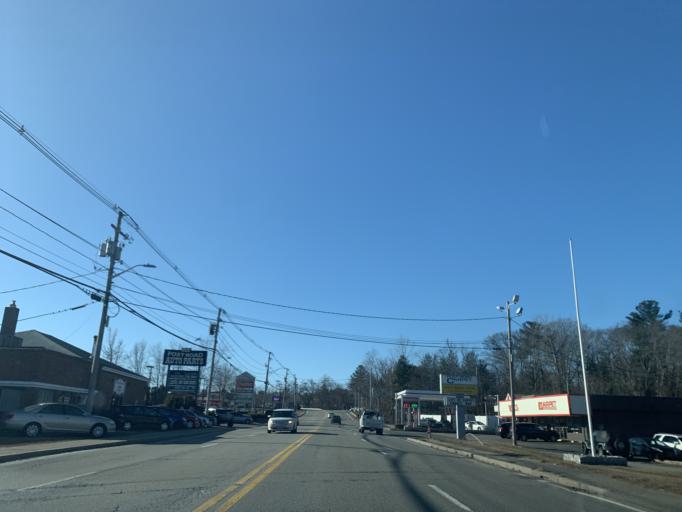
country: US
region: Massachusetts
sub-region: Worcester County
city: Southborough
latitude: 42.3507
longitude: -71.4979
